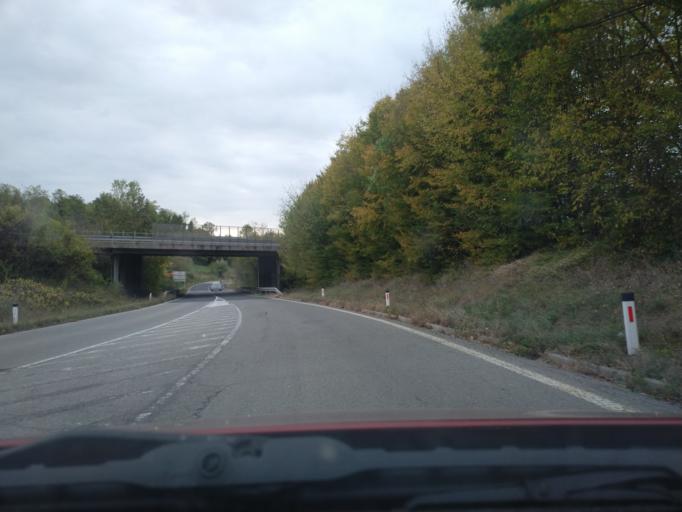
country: SI
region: Sempeter-Vrtojba
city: Sempeter pri Gorici
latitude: 45.9217
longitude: 13.6505
